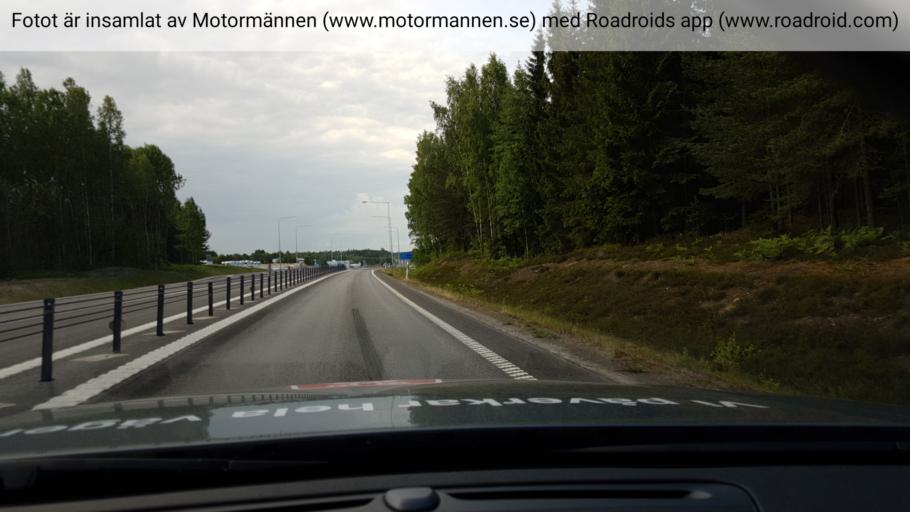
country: SE
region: OErebro
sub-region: Askersunds Kommun
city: Asbro
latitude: 59.0041
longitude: 15.0436
